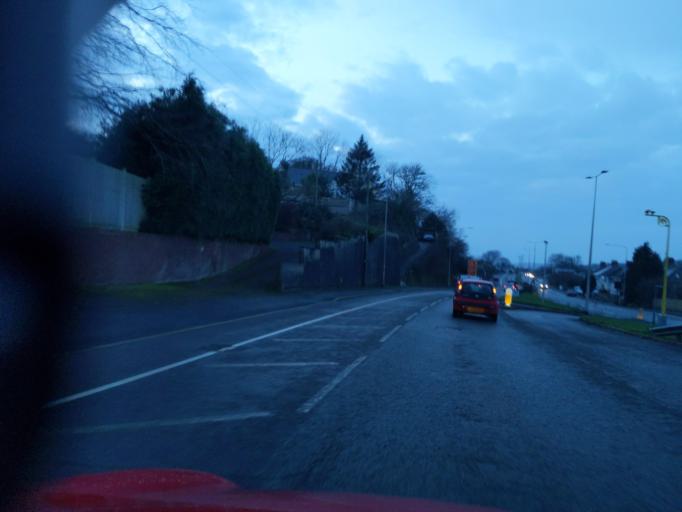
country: GB
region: England
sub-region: Plymouth
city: Plymstock
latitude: 50.3628
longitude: -4.0718
